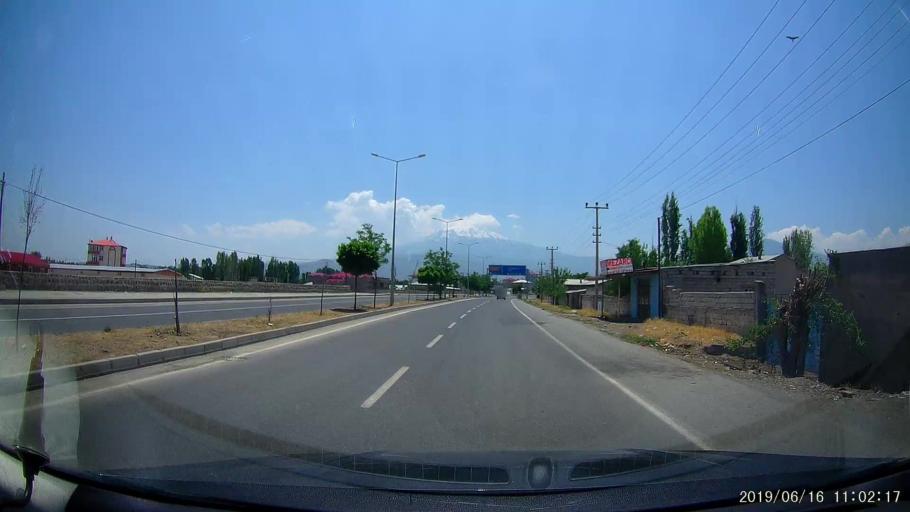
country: TR
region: Igdir
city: Igdir
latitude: 39.9080
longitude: 44.0582
